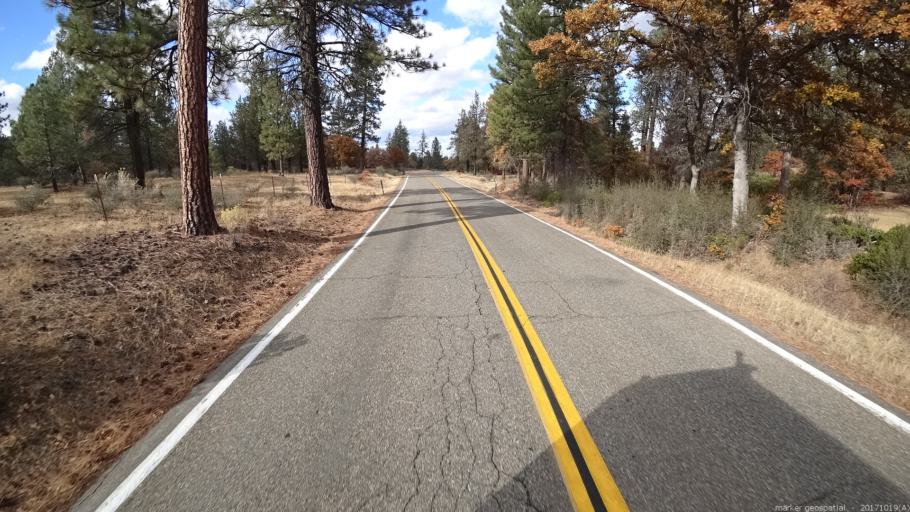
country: US
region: California
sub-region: Shasta County
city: Burney
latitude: 40.9525
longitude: -121.4408
